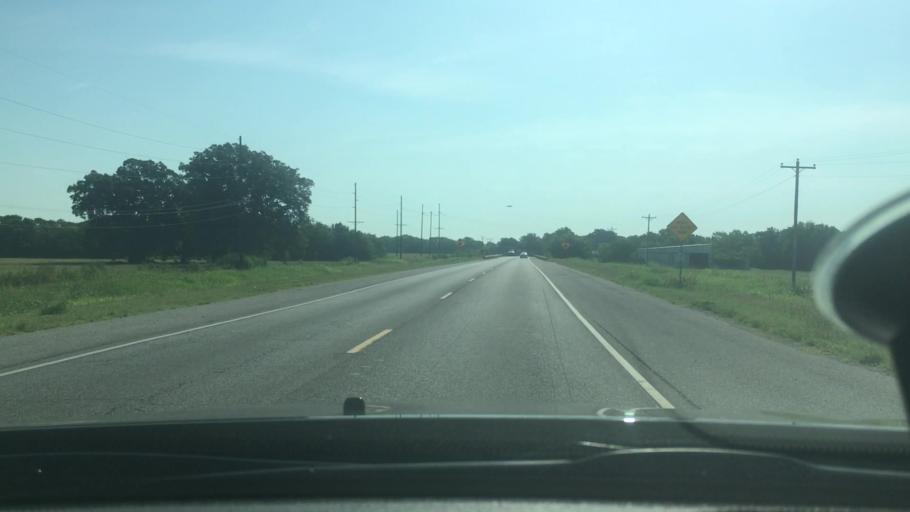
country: US
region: Oklahoma
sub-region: Garvin County
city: Wynnewood
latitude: 34.6516
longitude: -97.2070
